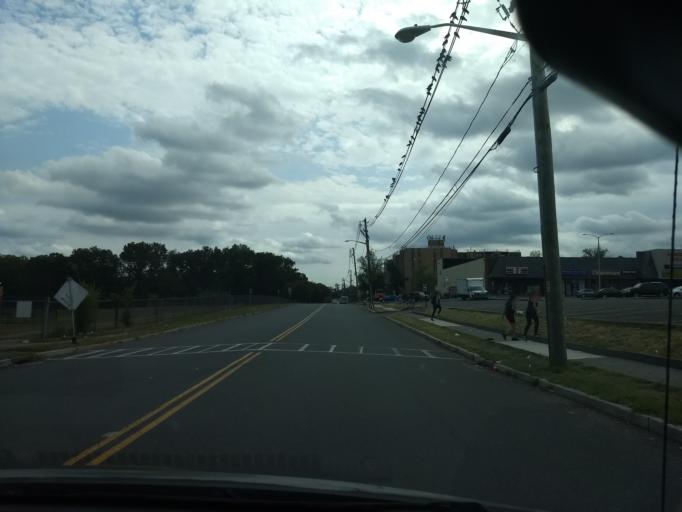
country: US
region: New York
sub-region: Rockland County
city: Monsey
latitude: 41.1080
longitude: -74.0580
